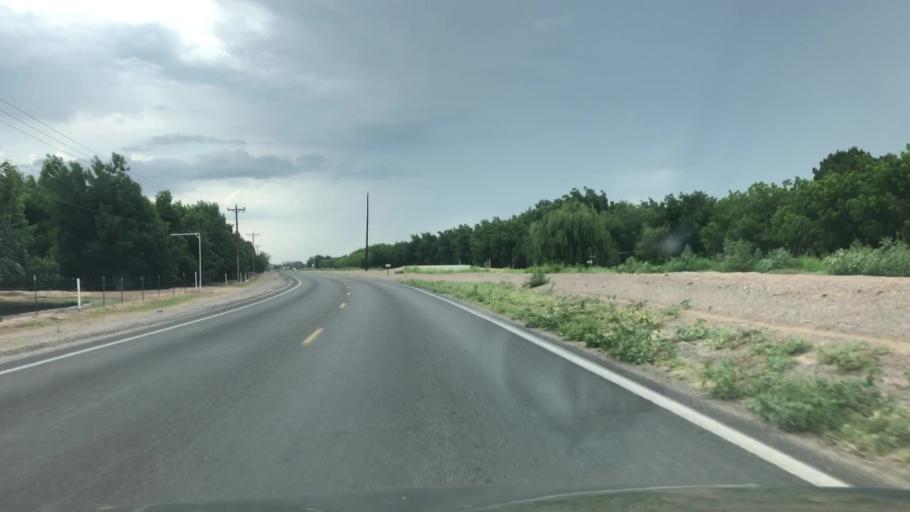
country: US
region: New Mexico
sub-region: Dona Ana County
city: La Union
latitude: 31.9915
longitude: -106.6515
